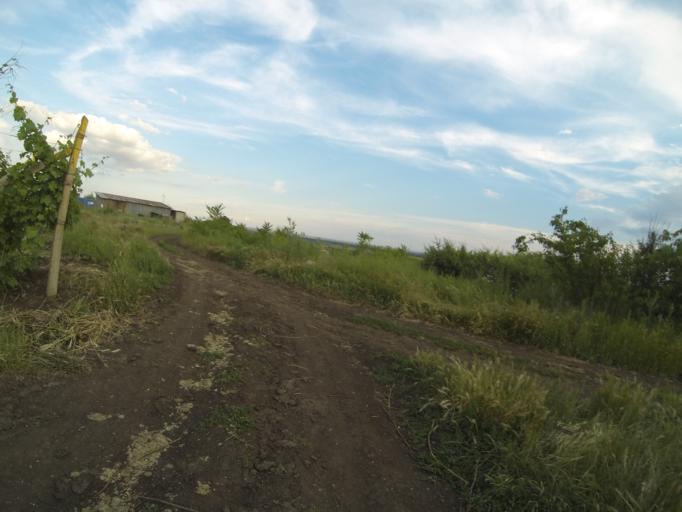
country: RO
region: Dolj
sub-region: Comuna Ceratu
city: Ceratu
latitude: 44.1114
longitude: 23.6817
